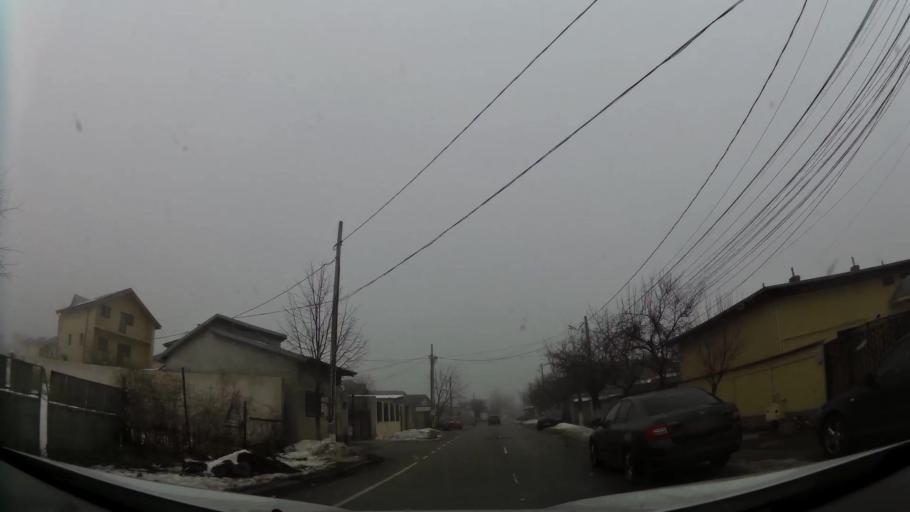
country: RO
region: Ilfov
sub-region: Comuna Chiajna
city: Chiajna
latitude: 44.4561
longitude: 25.9784
